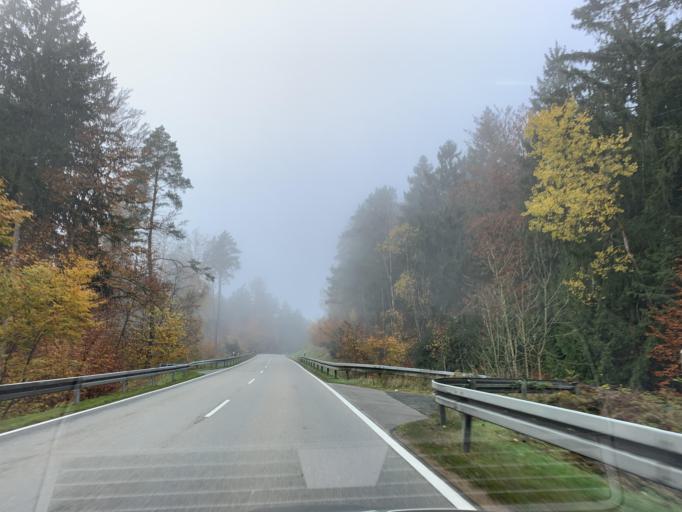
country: DE
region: Bavaria
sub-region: Upper Palatinate
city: Brunn
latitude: 49.2294
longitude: 12.1620
